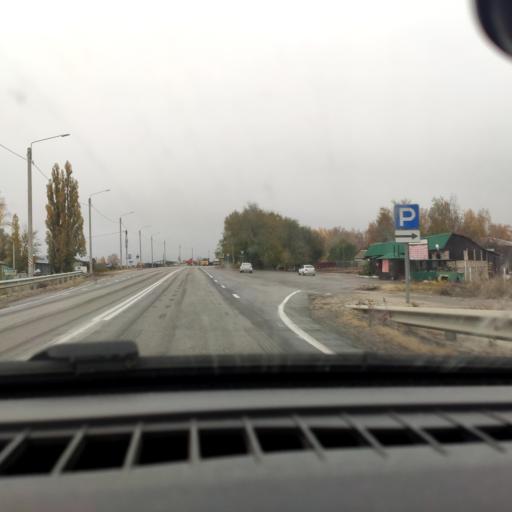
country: RU
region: Voronezj
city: Uryv-Pokrovka
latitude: 51.0425
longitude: 38.9822
